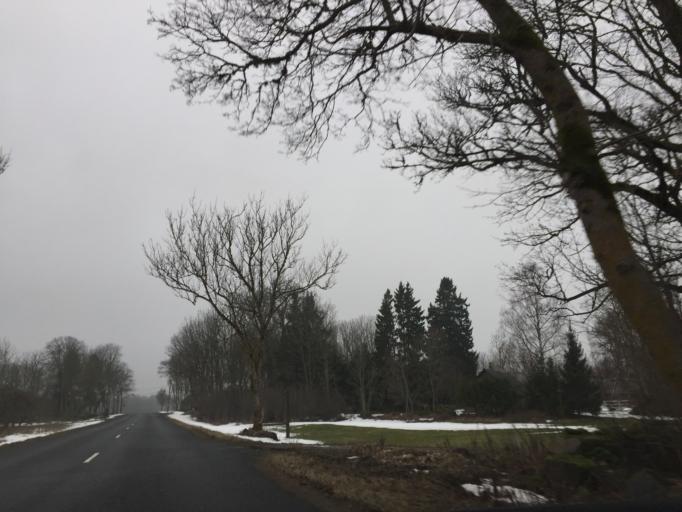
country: EE
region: Saare
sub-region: Orissaare vald
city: Orissaare
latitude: 58.3922
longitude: 22.8447
